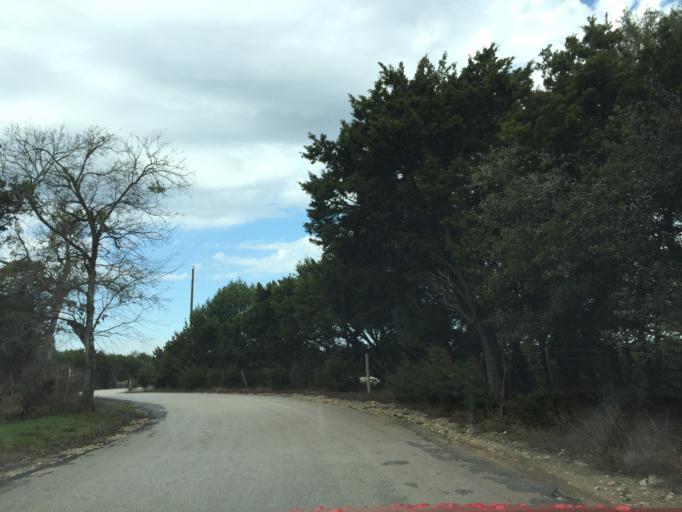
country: US
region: Texas
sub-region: Burnet County
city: Bertram
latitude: 30.6330
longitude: -98.0046
